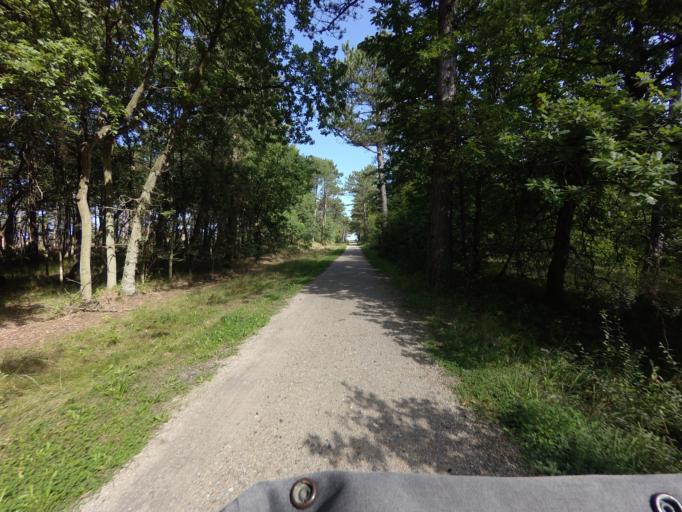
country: NL
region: Friesland
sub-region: Gemeente Terschelling
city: West-Terschelling
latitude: 53.3838
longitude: 5.2196
